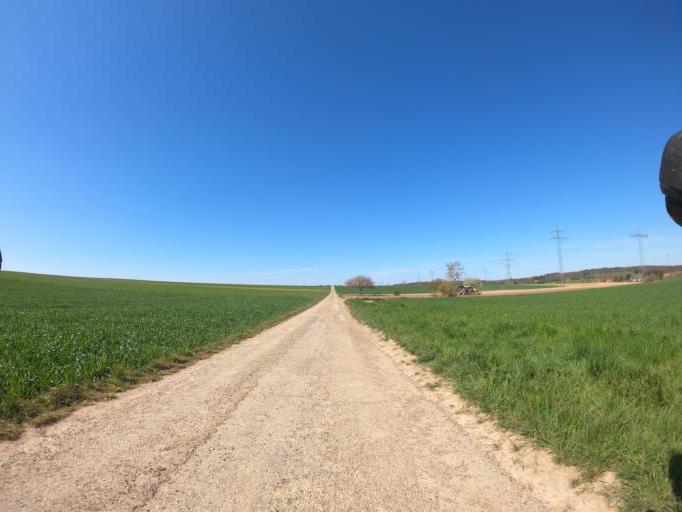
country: DE
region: Baden-Wuerttemberg
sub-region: Karlsruhe Region
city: Wiernsheim
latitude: 48.9039
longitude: 8.8383
